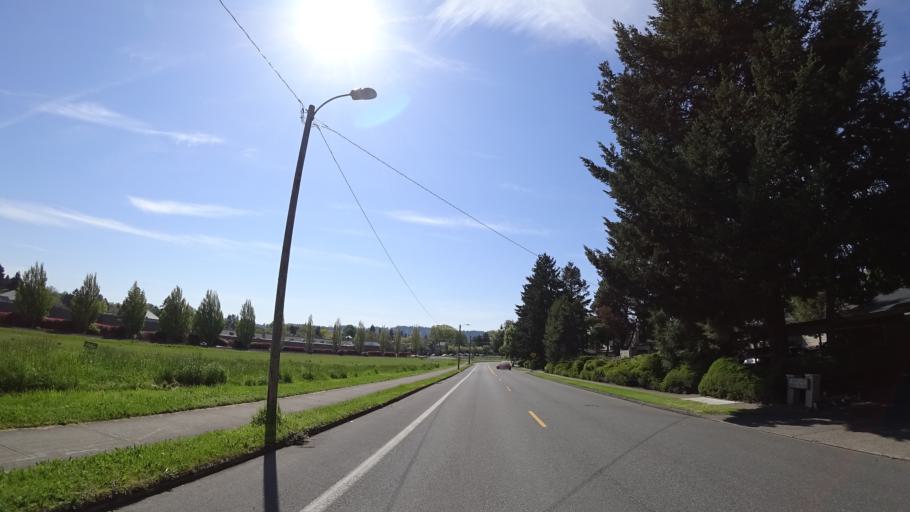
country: US
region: Oregon
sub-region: Clackamas County
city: Milwaukie
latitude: 45.4452
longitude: -122.6258
